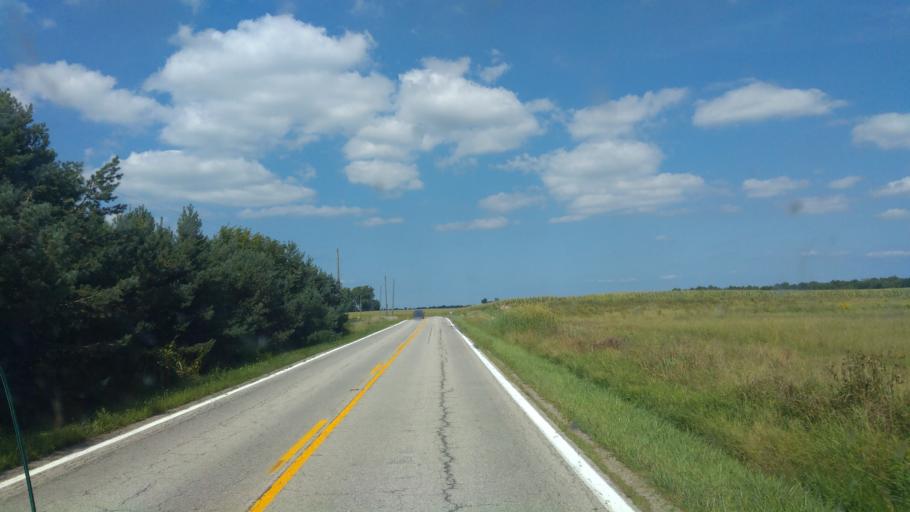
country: US
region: Ohio
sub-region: Union County
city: Marysville
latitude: 40.3523
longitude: -83.4558
